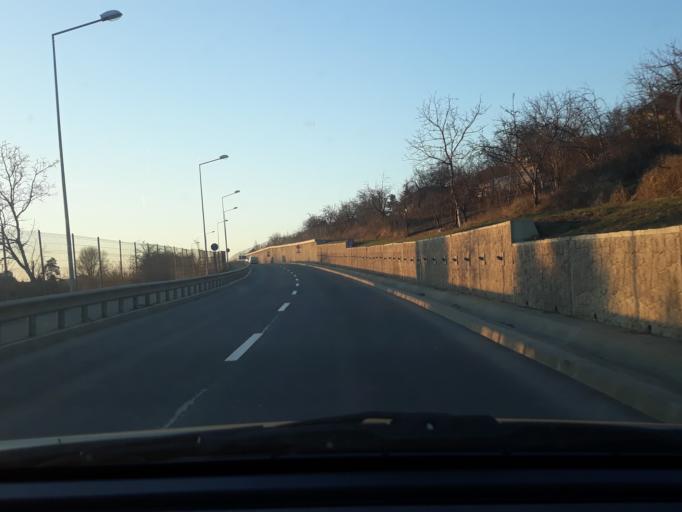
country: RO
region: Bihor
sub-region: Comuna Biharea
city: Oradea
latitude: 47.0595
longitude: 21.9467
